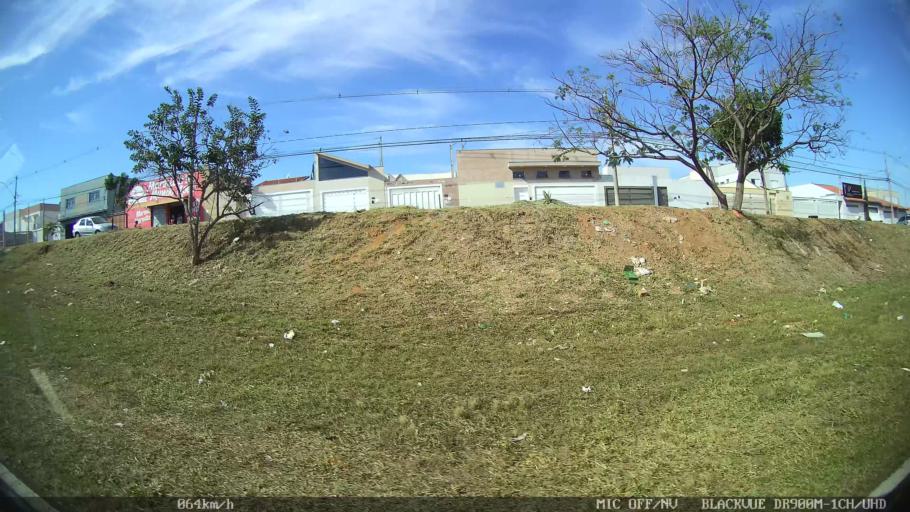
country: BR
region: Sao Paulo
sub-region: Franca
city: Franca
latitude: -20.5120
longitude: -47.4403
